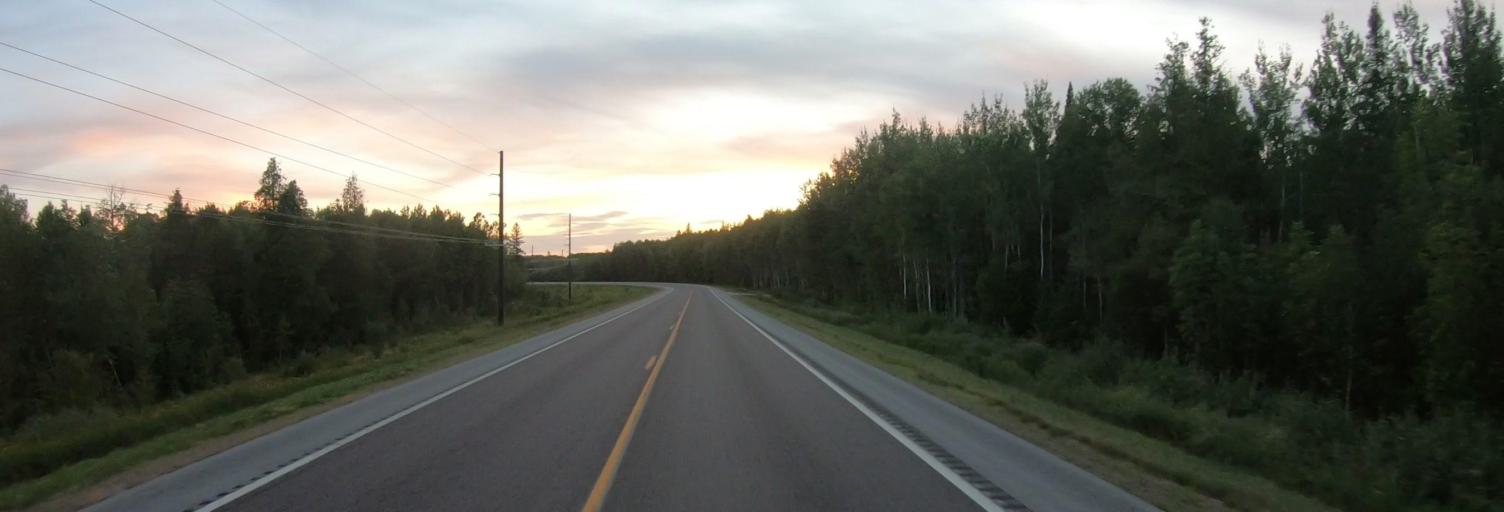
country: US
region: Minnesota
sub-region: Saint Louis County
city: Virginia
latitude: 47.8589
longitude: -92.4586
